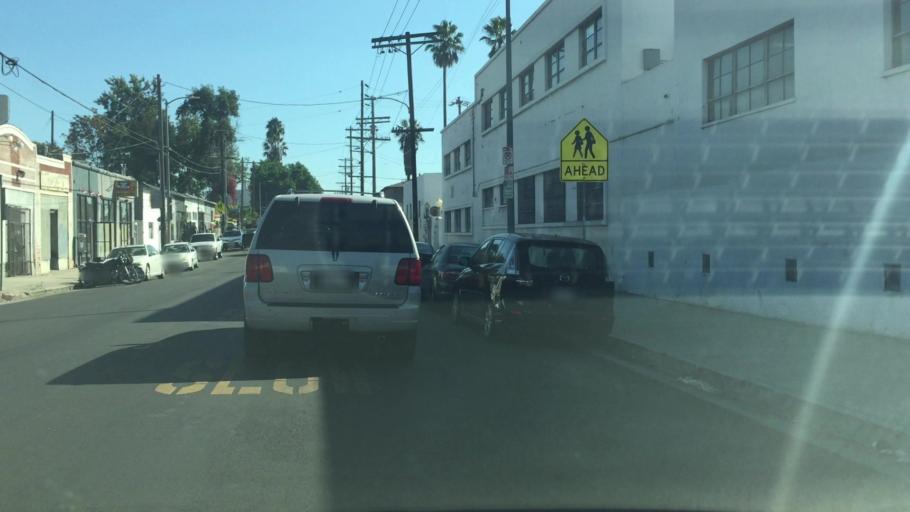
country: US
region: California
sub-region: Los Angeles County
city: Silver Lake
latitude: 34.0826
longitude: -118.2845
